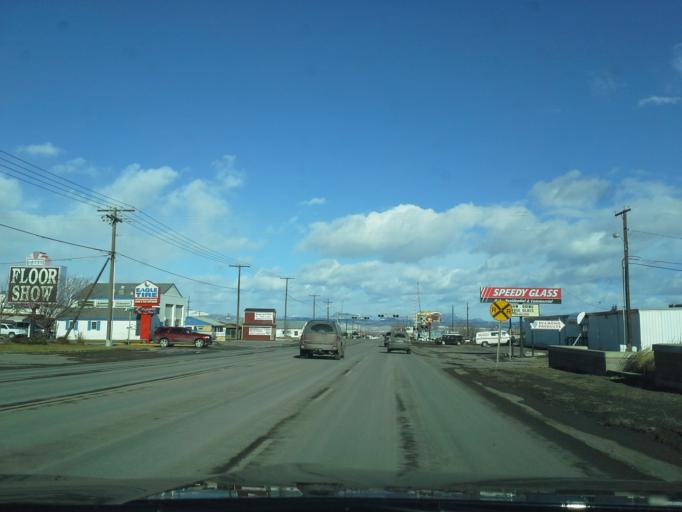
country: US
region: Montana
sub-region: Lewis and Clark County
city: Helena
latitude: 46.5994
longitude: -112.0205
